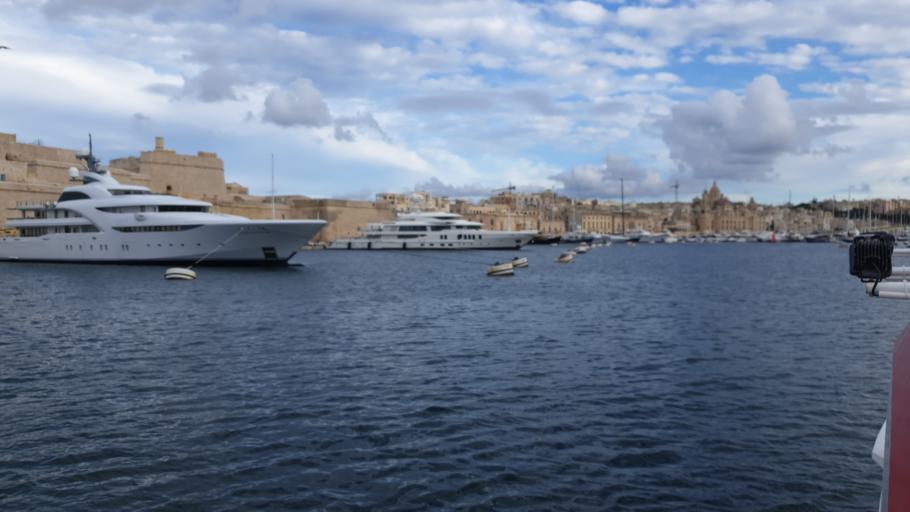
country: MT
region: Il-Birgu
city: Vittoriosa
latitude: 35.8915
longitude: 14.5154
